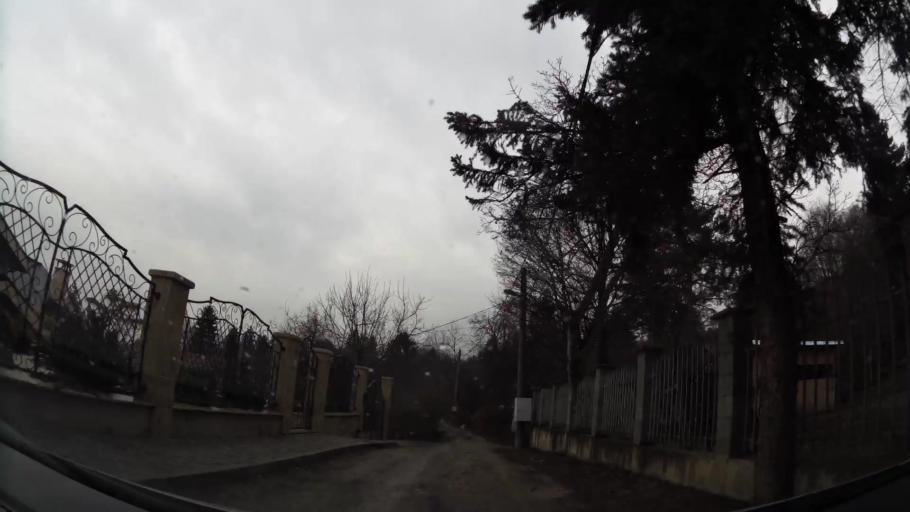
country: BG
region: Sofia-Capital
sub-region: Stolichna Obshtina
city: Sofia
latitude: 42.6014
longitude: 23.3864
